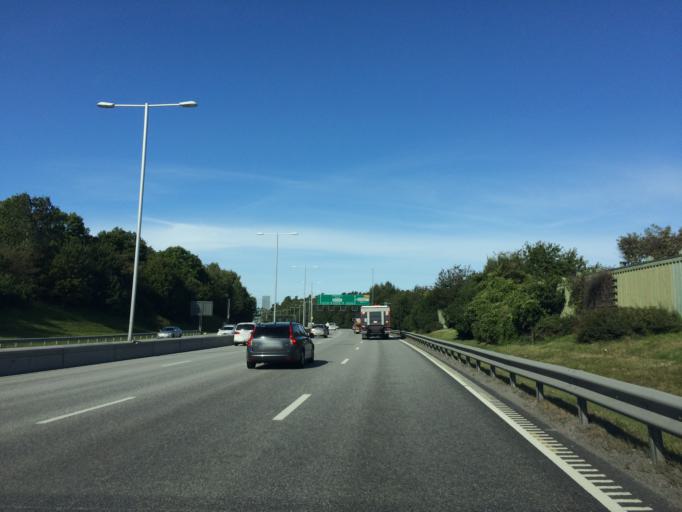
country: SE
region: Stockholm
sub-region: Solna Kommun
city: Solna
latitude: 59.3877
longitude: 18.0019
